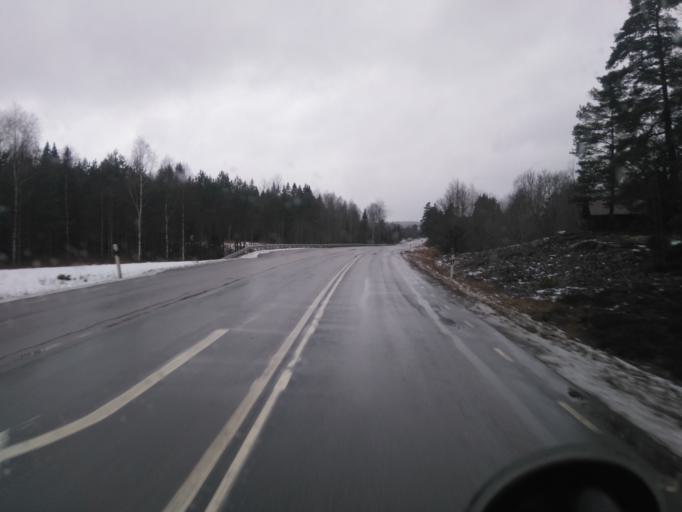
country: SE
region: Joenkoeping
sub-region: Eksjo Kommun
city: Haljarp
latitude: 57.6310
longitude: 15.4306
